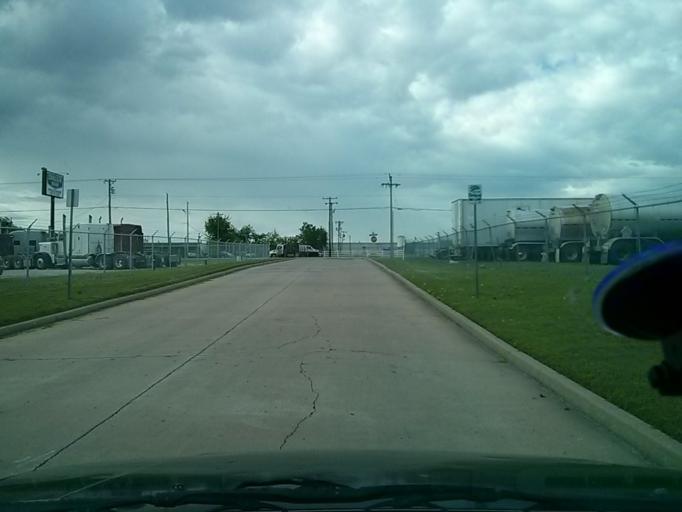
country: US
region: Oklahoma
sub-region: Rogers County
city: Catoosa
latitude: 36.1615
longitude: -95.8389
